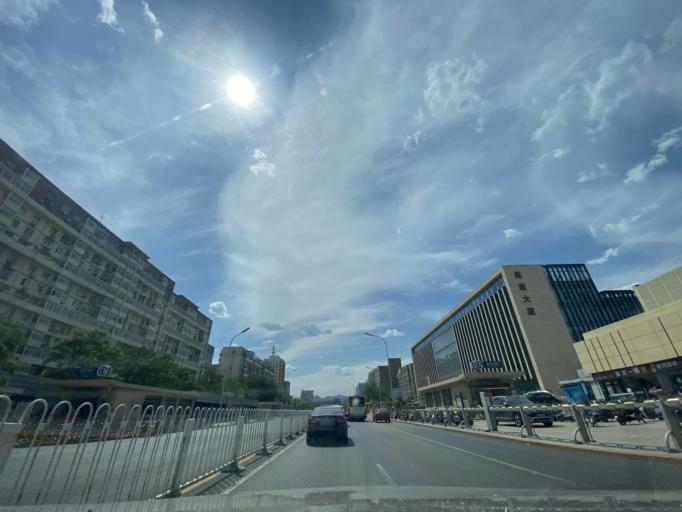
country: CN
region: Beijing
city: Lugu
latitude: 39.9062
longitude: 116.1853
